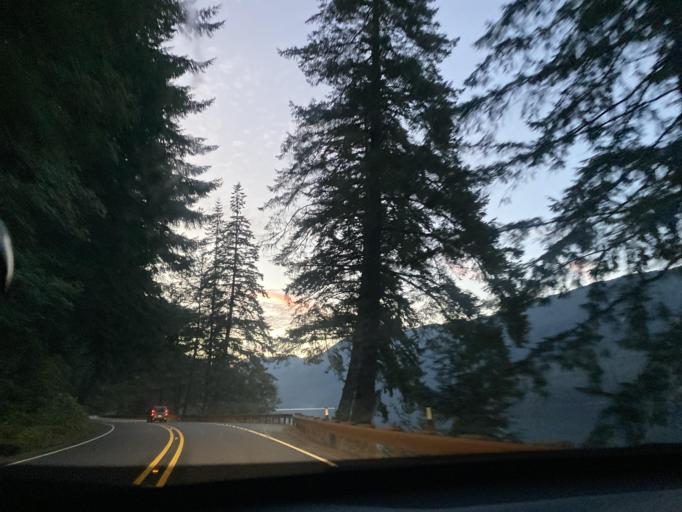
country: CA
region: British Columbia
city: Sooke
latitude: 48.0491
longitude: -123.8557
